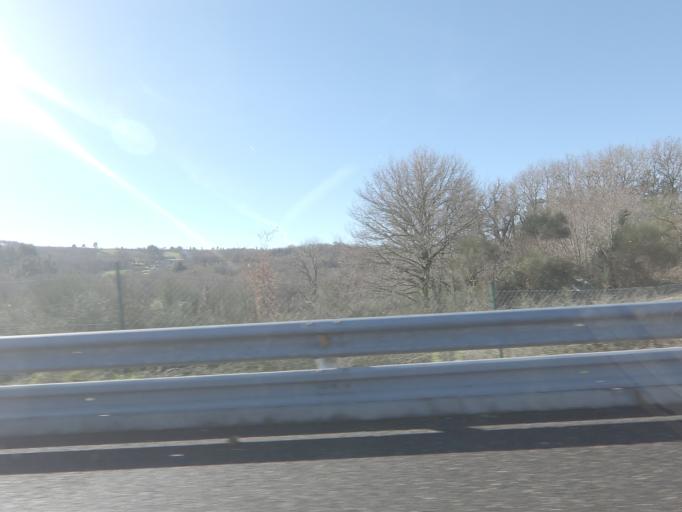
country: ES
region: Galicia
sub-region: Provincia de Pontevedra
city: Dozon
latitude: 42.5682
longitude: -8.0561
